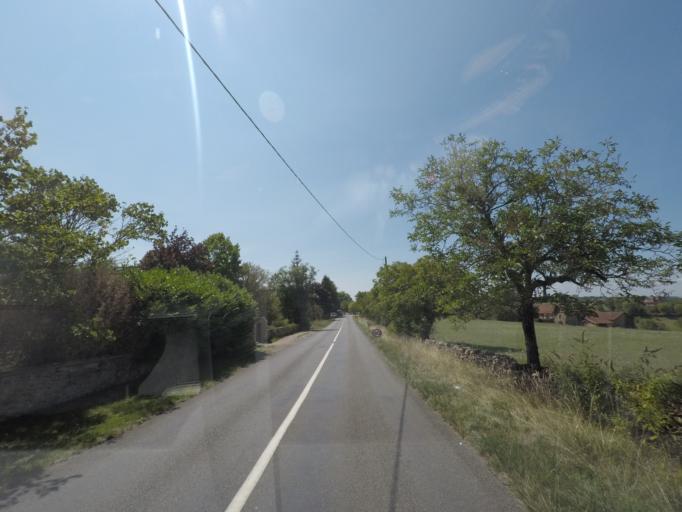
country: FR
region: Midi-Pyrenees
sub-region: Departement de l'Aveyron
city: Capdenac-Gare
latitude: 44.6082
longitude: 2.0740
